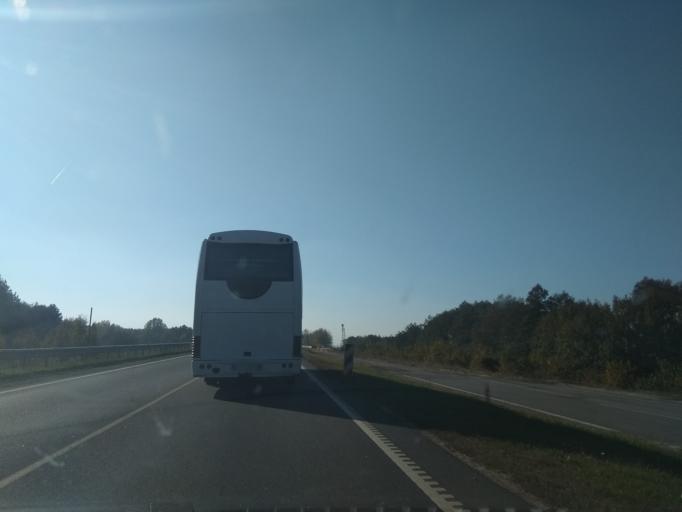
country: BY
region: Brest
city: Zhabinka
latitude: 52.1361
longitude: 23.9510
